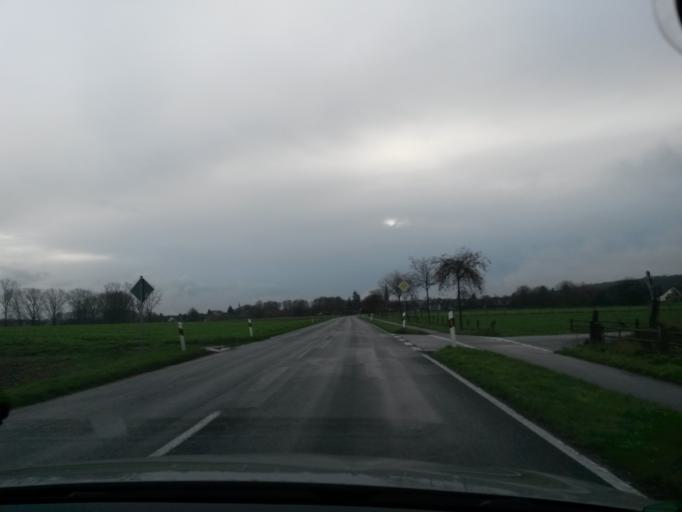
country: DE
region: North Rhine-Westphalia
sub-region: Regierungsbezirk Dusseldorf
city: Alpen
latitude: 51.5836
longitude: 6.5020
